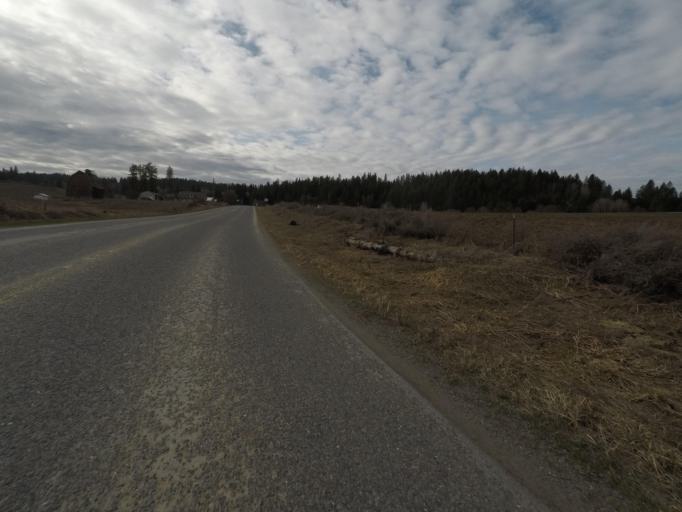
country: US
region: Washington
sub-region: Stevens County
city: Colville
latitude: 48.5172
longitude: -117.8685
